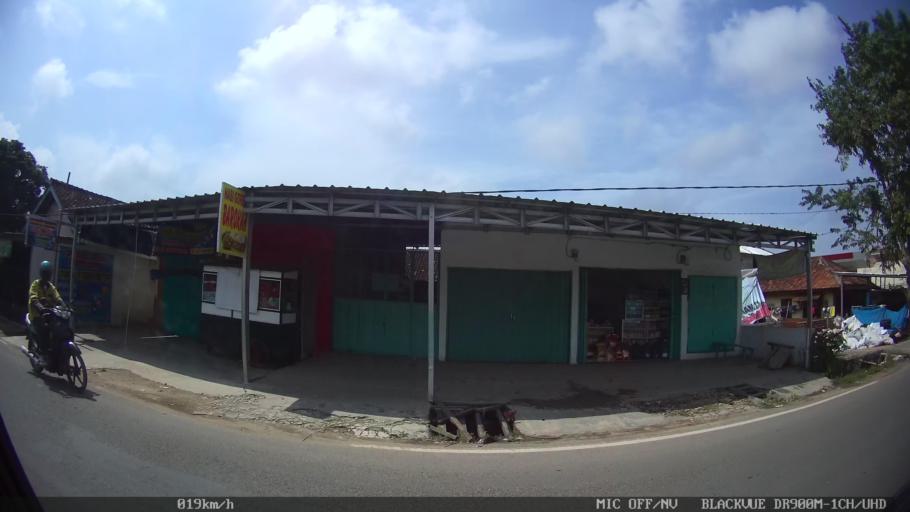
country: ID
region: Lampung
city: Kedaton
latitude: -5.3629
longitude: 105.2781
